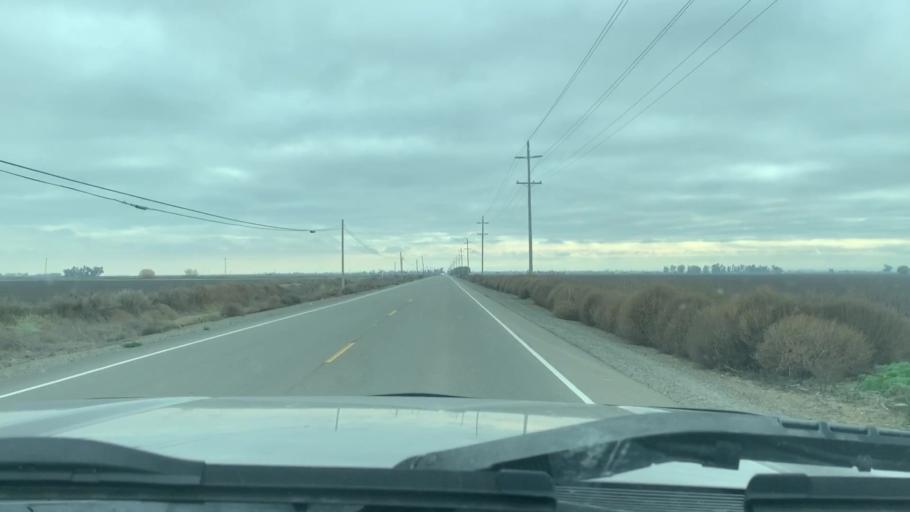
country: US
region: California
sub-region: Merced County
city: Los Banos
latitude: 37.1250
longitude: -120.8348
